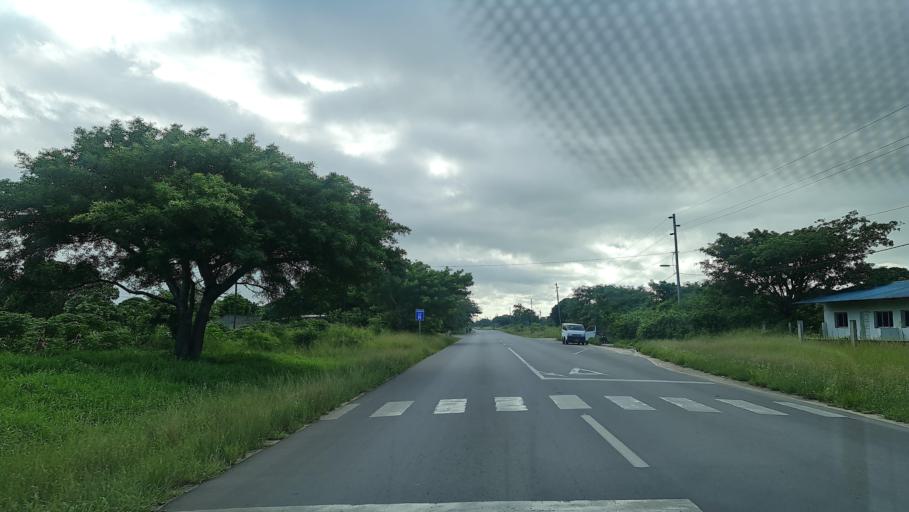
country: MZ
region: Maputo
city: Manhica
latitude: -25.4105
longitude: 32.7475
